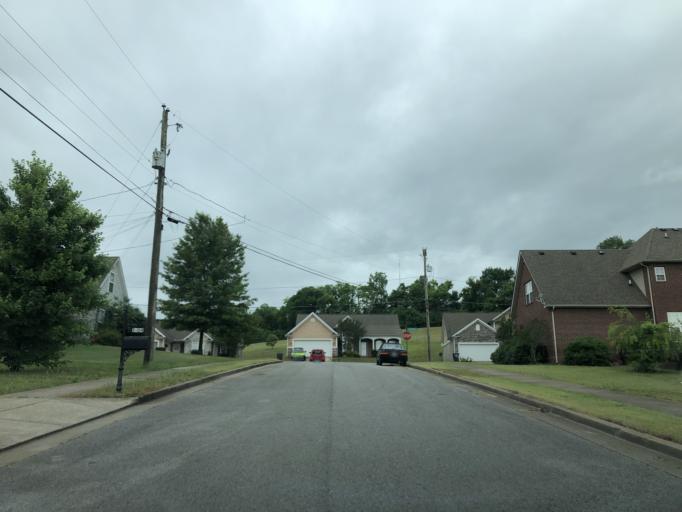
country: US
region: Tennessee
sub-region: Davidson County
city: Goodlettsville
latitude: 36.2751
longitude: -86.7685
